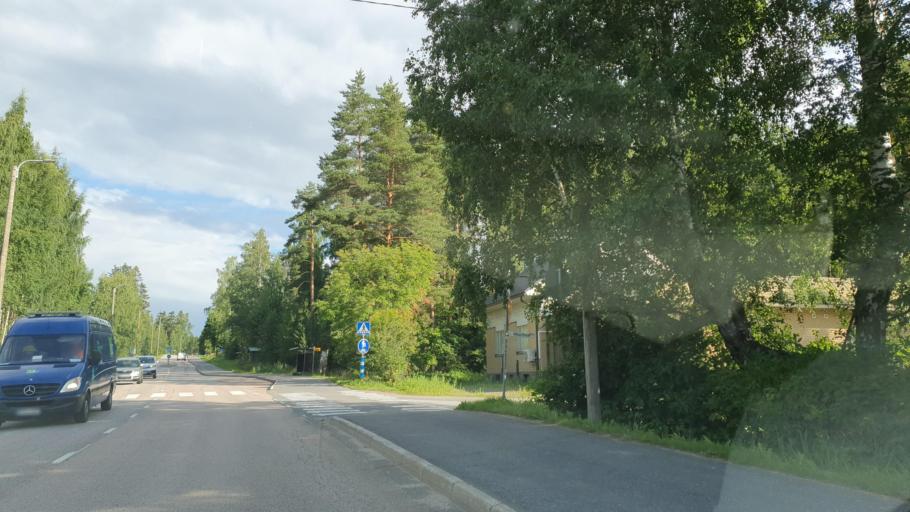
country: FI
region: Central Finland
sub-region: Jyvaeskylae
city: Saeynaetsalo
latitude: 62.1569
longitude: 25.7549
